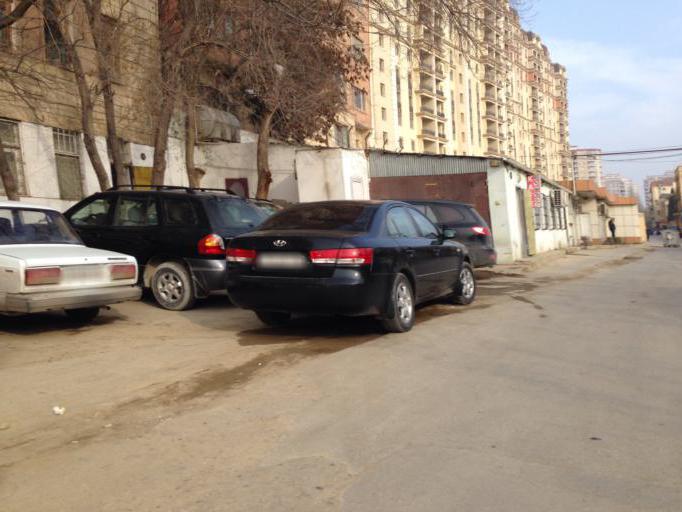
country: AZ
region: Baki
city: Baku
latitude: 40.3991
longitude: 49.8621
